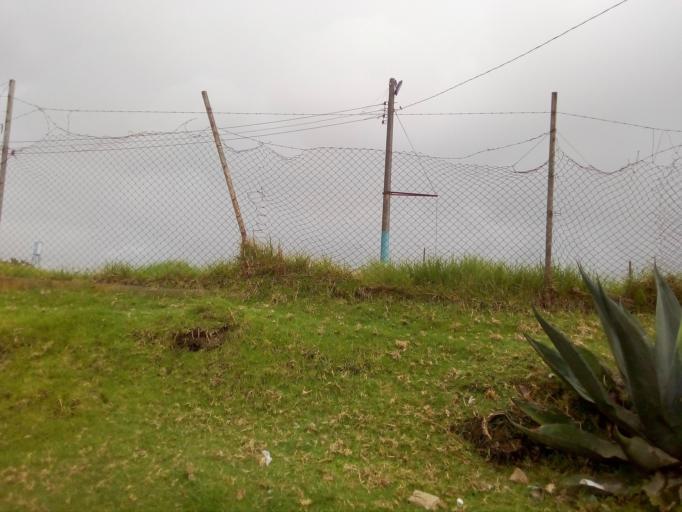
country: GT
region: Quetzaltenango
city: Olintepeque
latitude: 14.8606
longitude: -91.5032
